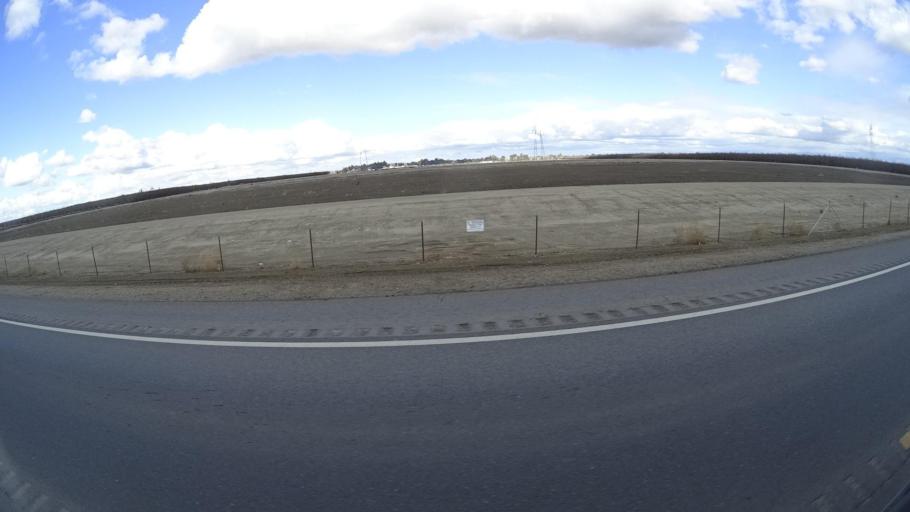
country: US
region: California
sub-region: Kern County
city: Greenfield
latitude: 35.2088
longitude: -119.0860
